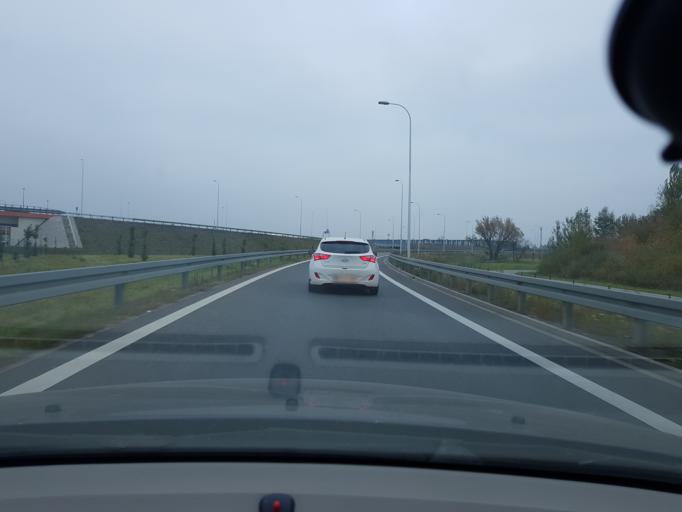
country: PL
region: Masovian Voivodeship
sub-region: Powiat pruszkowski
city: Nowe Grocholice
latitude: 52.1704
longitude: 20.9114
